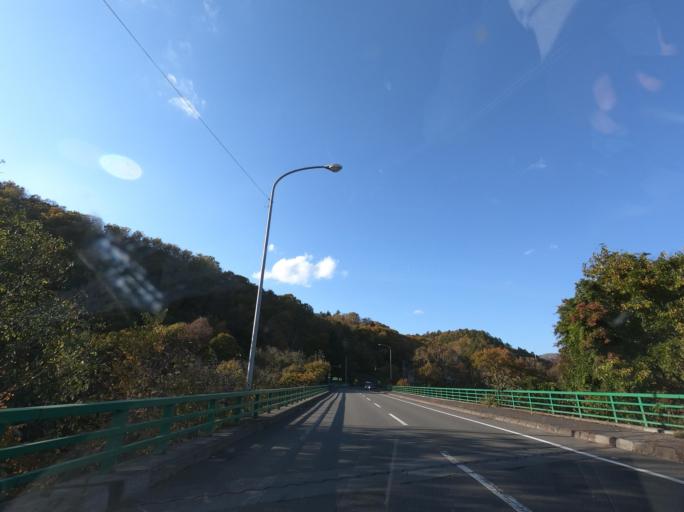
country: JP
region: Hokkaido
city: Iwamizawa
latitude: 42.9991
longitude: 142.0056
